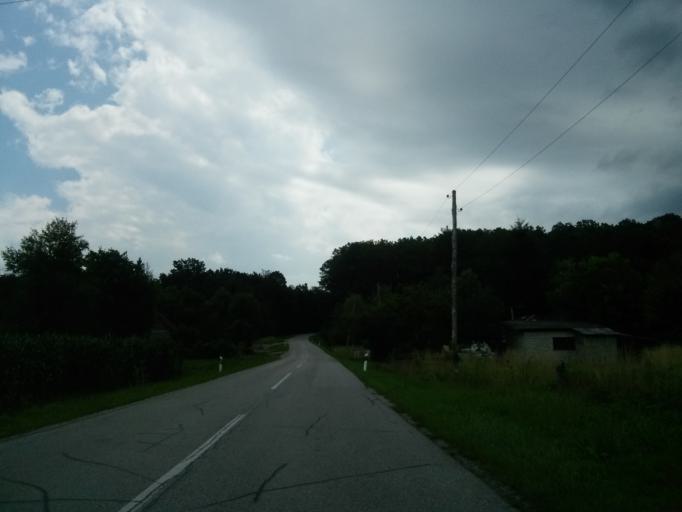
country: HR
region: Sisacko-Moslavacka
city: Gvozd
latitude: 45.3180
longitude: 15.9604
